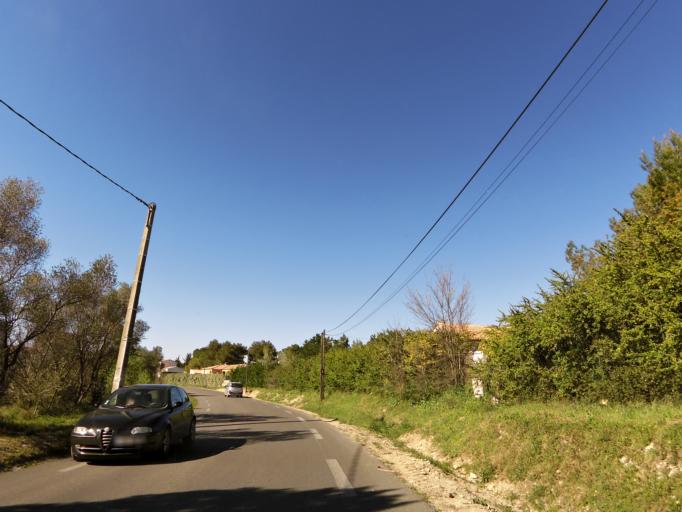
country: FR
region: Languedoc-Roussillon
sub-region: Departement du Gard
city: Aubais
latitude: 43.7422
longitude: 4.1456
